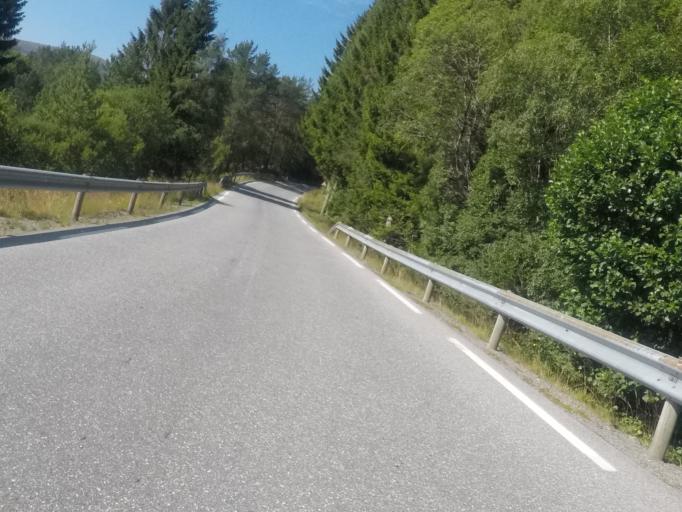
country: NO
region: Sogn og Fjordane
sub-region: Bremanger
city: Svelgen
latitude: 61.7383
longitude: 5.1819
